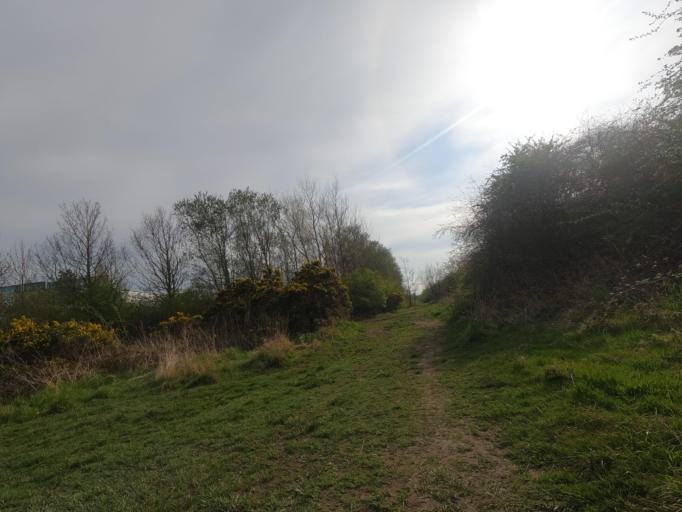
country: GB
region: England
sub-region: Newcastle upon Tyne
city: Hazlerigg
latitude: 55.0365
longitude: -1.6503
